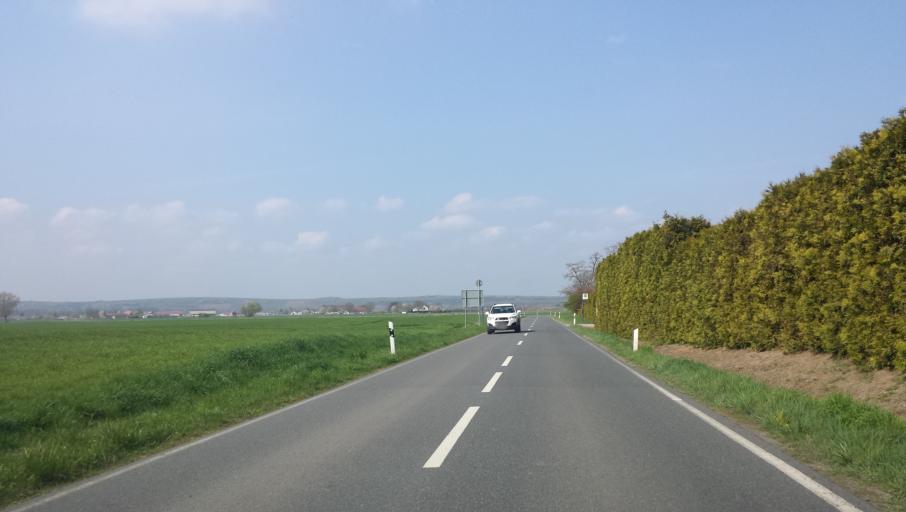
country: DE
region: Hesse
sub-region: Regierungsbezirk Darmstadt
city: Trebur
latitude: 49.8945
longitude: 8.3990
